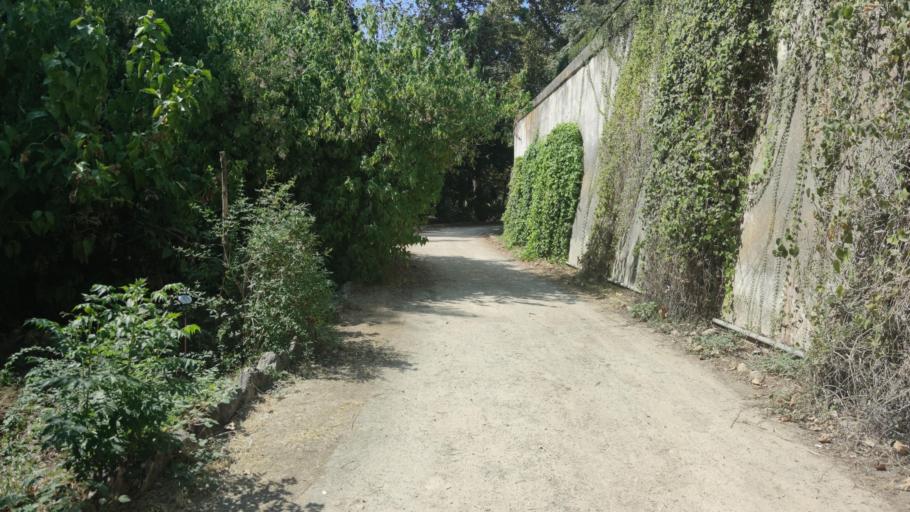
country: IT
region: Sicily
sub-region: Palermo
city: Palermo
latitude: 38.1102
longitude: 13.3752
